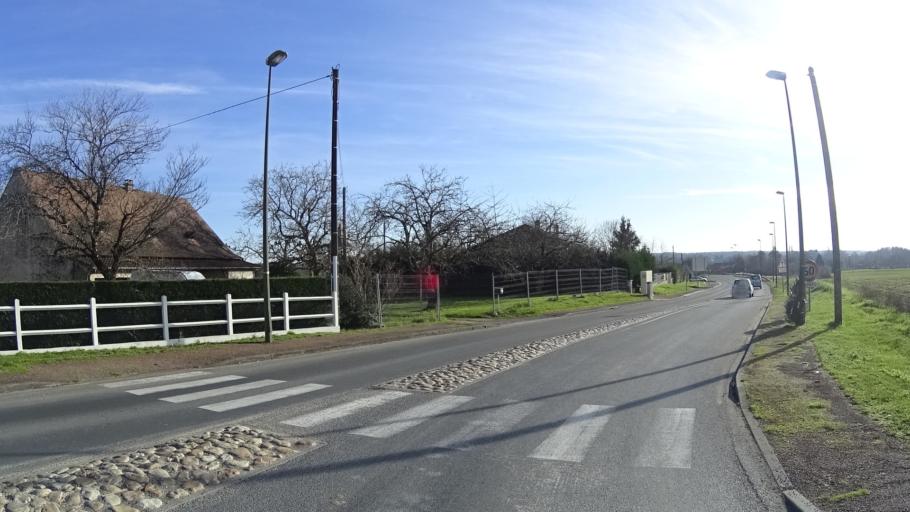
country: FR
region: Aquitaine
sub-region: Departement de la Dordogne
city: Mussidan
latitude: 45.0538
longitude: 0.3627
